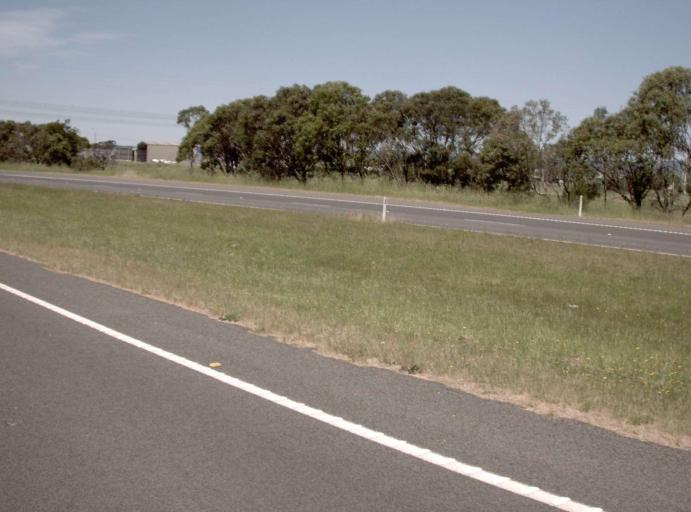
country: AU
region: Victoria
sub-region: Latrobe
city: Morwell
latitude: -38.2453
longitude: 146.4328
